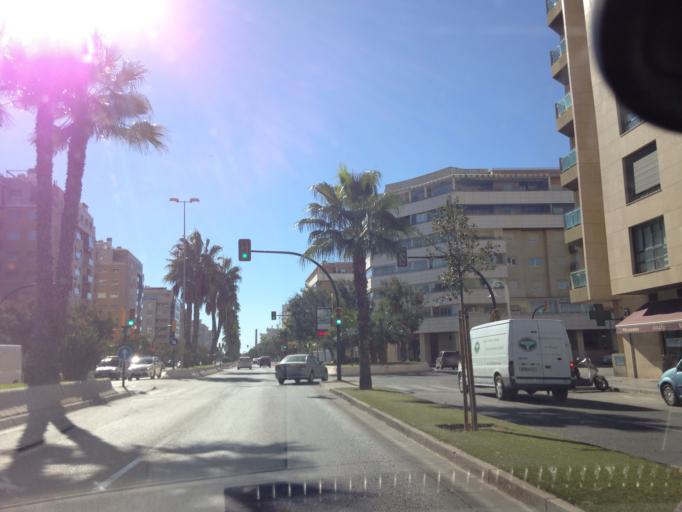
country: ES
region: Andalusia
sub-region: Provincia de Malaga
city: Malaga
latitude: 36.6947
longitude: -4.4402
